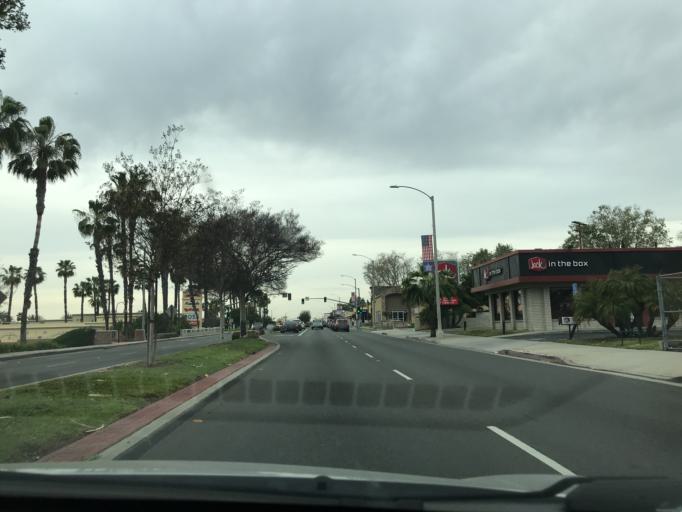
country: US
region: California
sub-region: Los Angeles County
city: South Whittier
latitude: 33.9614
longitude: -118.0297
